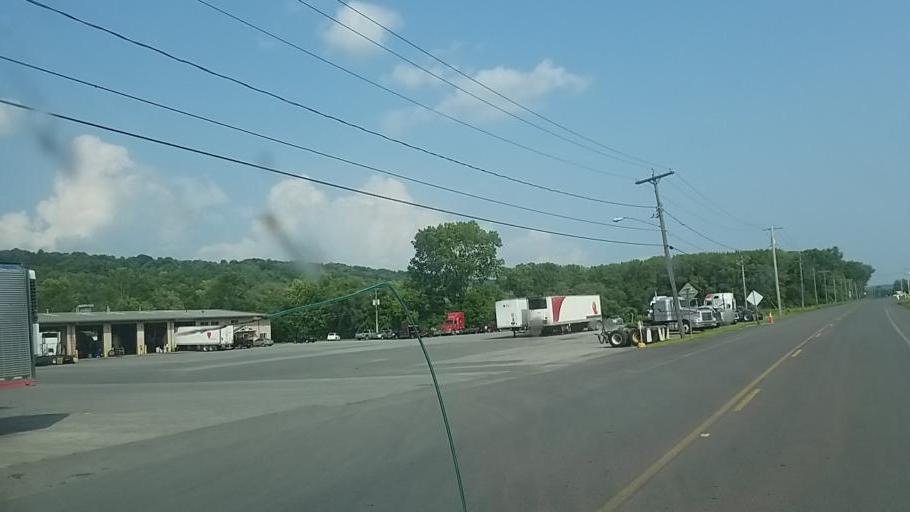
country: US
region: New York
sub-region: Montgomery County
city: Fonda
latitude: 42.9479
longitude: -74.3559
